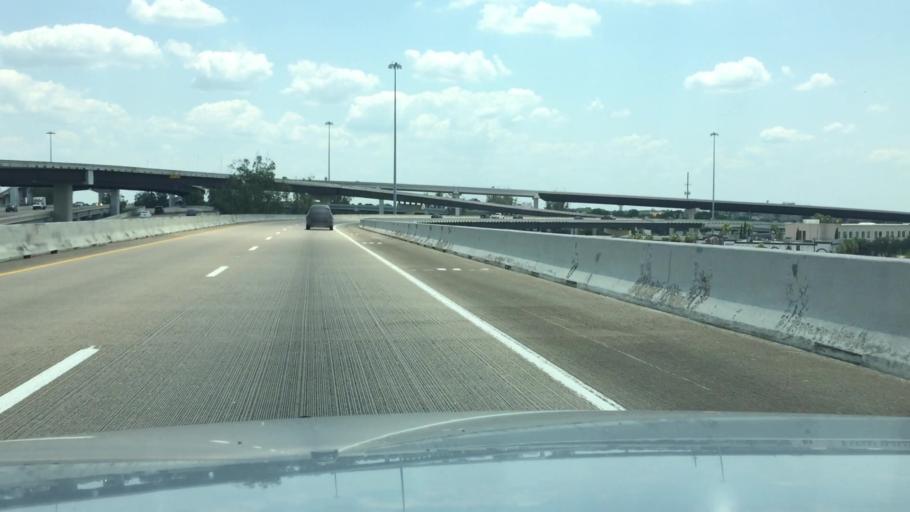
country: US
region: Texas
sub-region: Fort Bend County
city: Meadows Place
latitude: 29.6633
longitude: -95.5595
